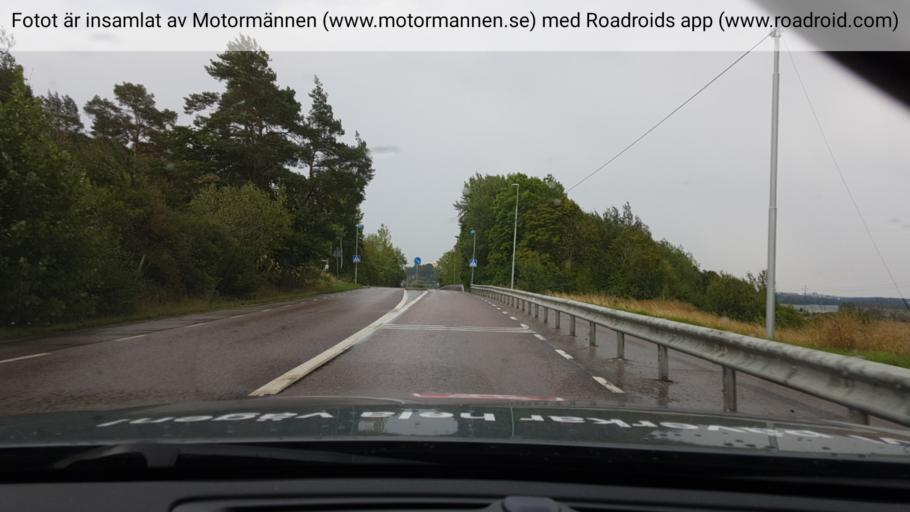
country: SE
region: Stockholm
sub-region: Upplands-Bro Kommun
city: Kungsaengen
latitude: 59.4784
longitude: 17.7194
